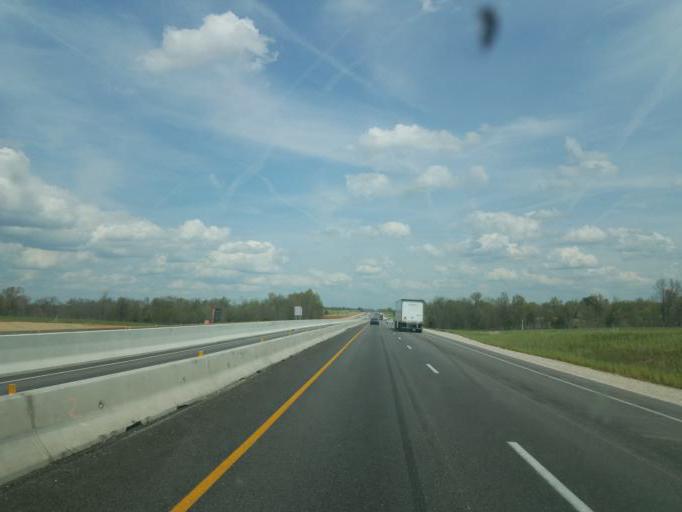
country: US
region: Kentucky
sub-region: Larue County
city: Hodgenville
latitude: 37.5394
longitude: -85.8809
